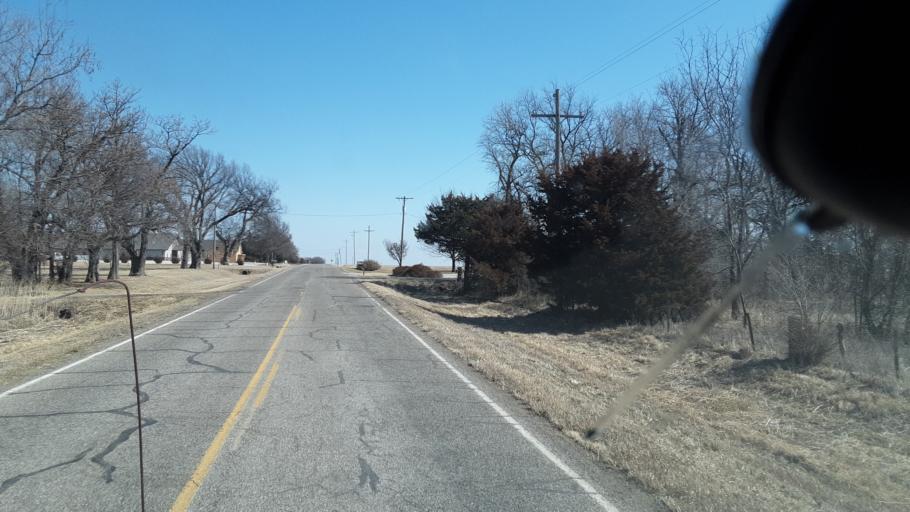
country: US
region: Kansas
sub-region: Reno County
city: South Hutchinson
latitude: 37.9700
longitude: -98.0173
